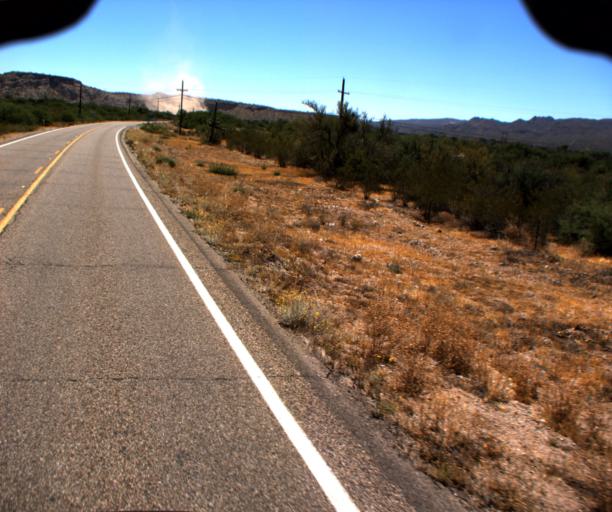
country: US
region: Arizona
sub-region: Pinal County
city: Kearny
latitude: 33.0507
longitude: -110.8931
